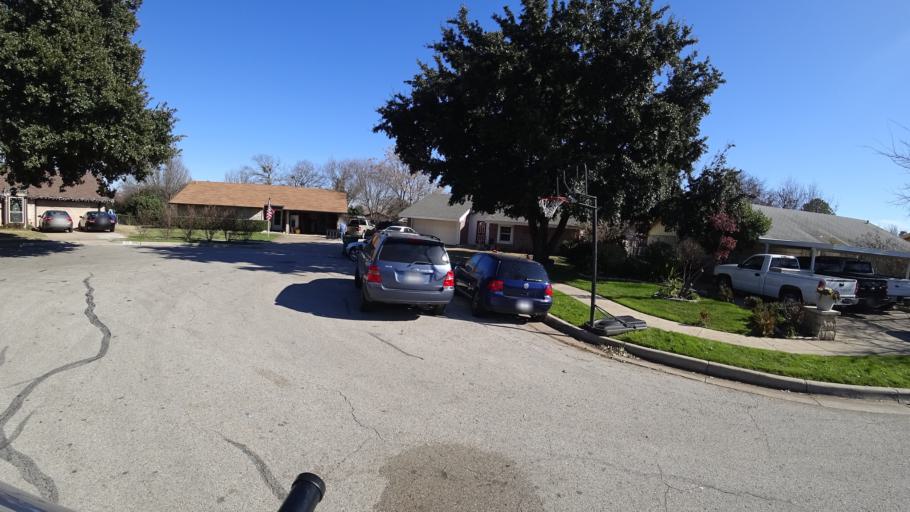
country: US
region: Texas
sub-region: Denton County
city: Lewisville
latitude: 33.0339
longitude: -97.0184
